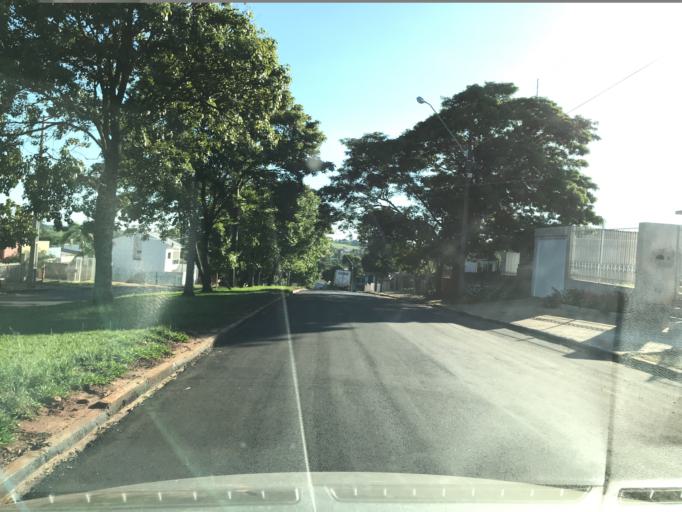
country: BR
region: Parana
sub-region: Ipora
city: Ipora
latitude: -24.0001
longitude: -53.7125
